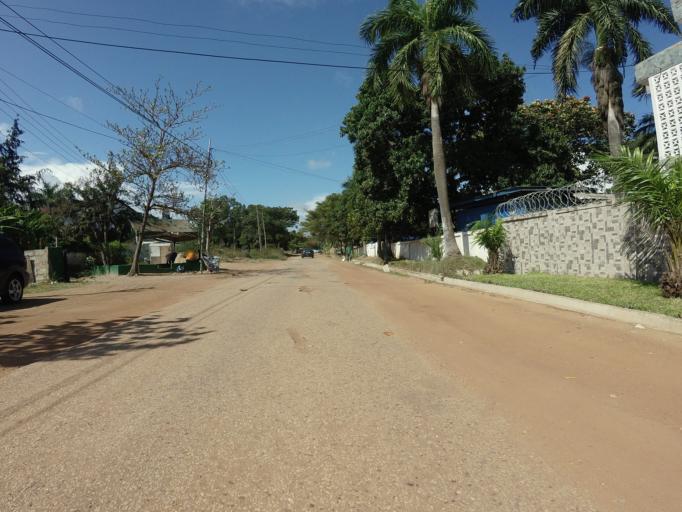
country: GH
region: Greater Accra
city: Accra
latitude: 5.5701
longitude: -0.1725
